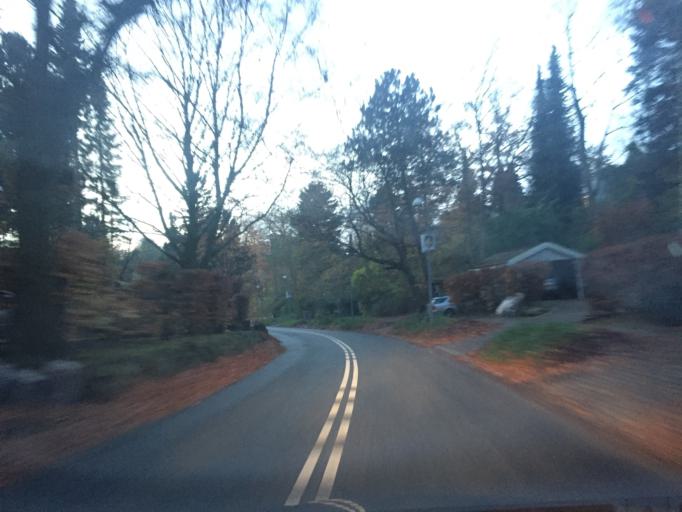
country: DK
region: Capital Region
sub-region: Rudersdal Kommune
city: Trorod
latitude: 55.7982
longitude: 12.5407
